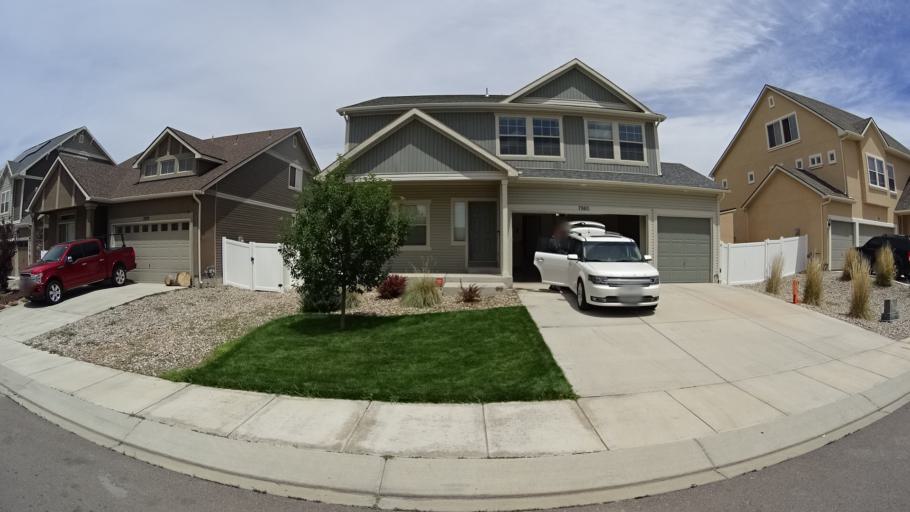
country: US
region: Colorado
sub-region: El Paso County
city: Fountain
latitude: 38.6957
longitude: -104.6794
